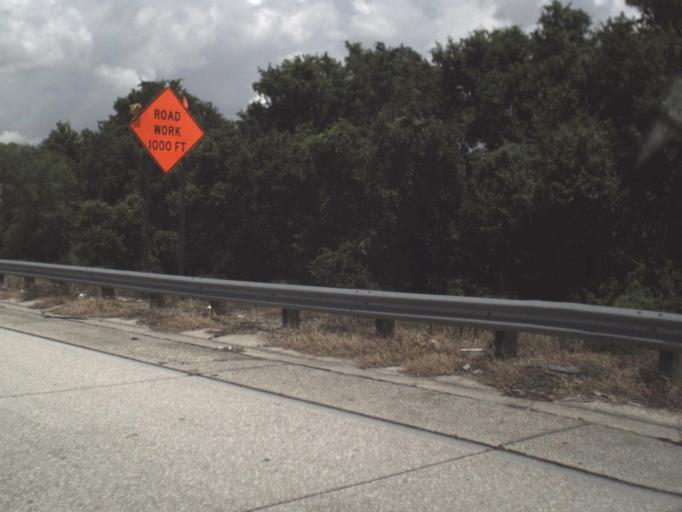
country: US
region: Florida
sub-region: Hillsborough County
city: Mango
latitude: 27.9476
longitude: -82.3283
